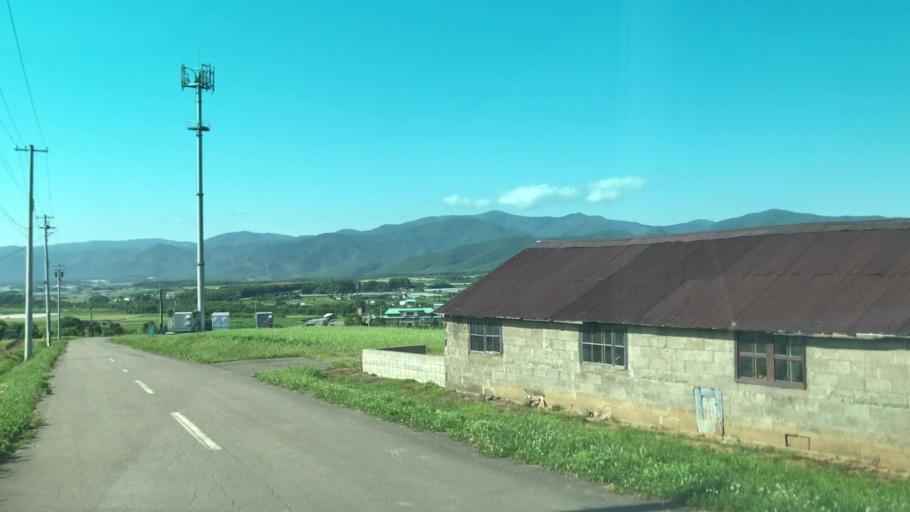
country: JP
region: Hokkaido
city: Iwanai
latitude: 42.9731
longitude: 140.6109
